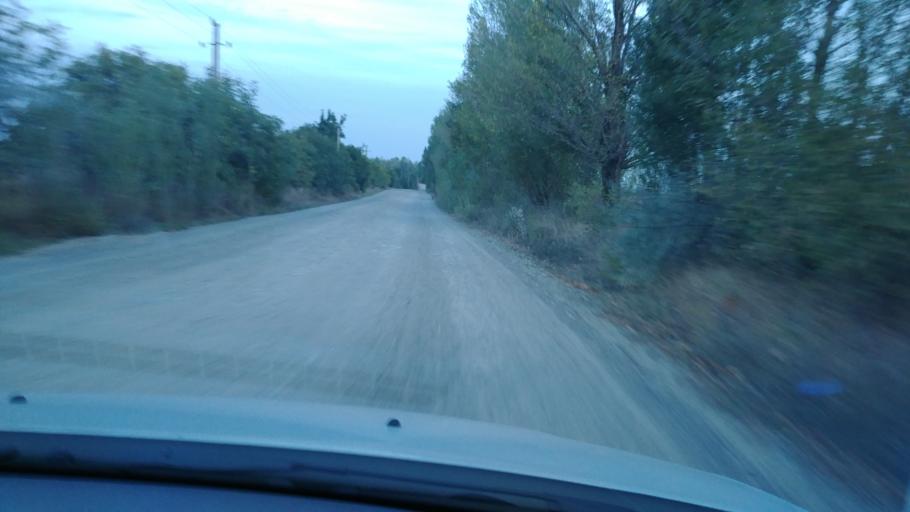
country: MD
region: Rezina
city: Saharna
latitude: 47.6794
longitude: 28.9193
